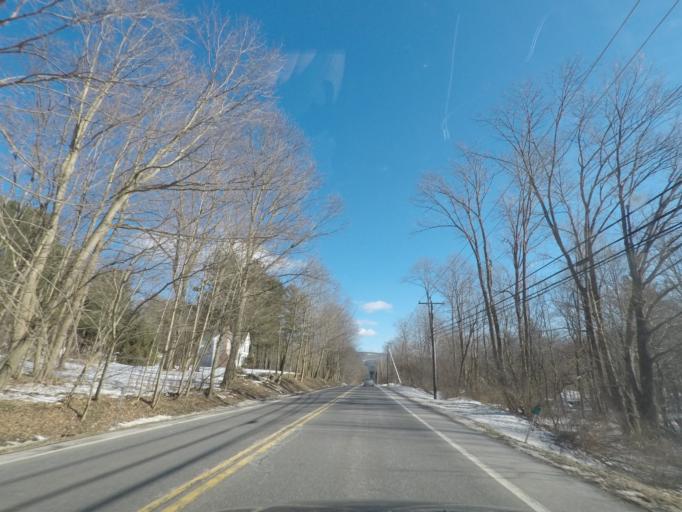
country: US
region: New York
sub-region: Columbia County
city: Chatham
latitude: 42.3177
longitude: -73.4849
